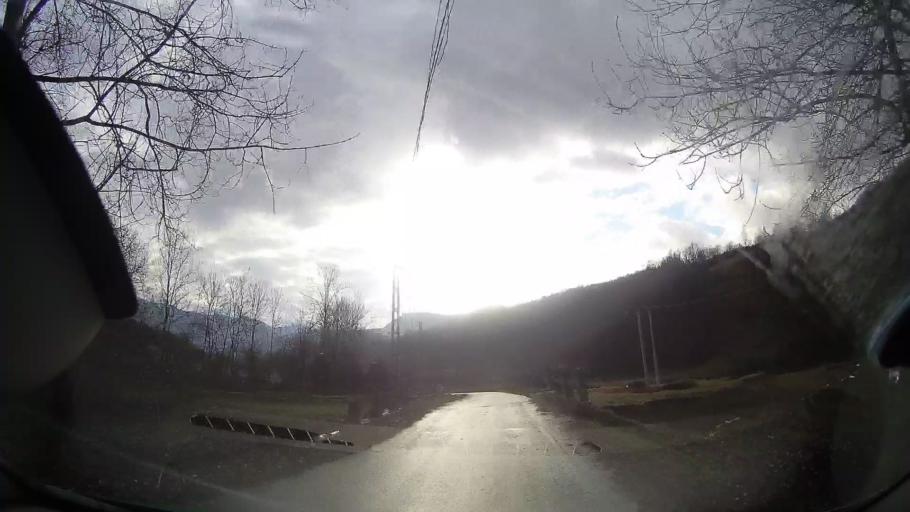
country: RO
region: Alba
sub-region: Comuna Ocolis
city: Ocolis
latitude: 46.4936
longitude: 23.4567
